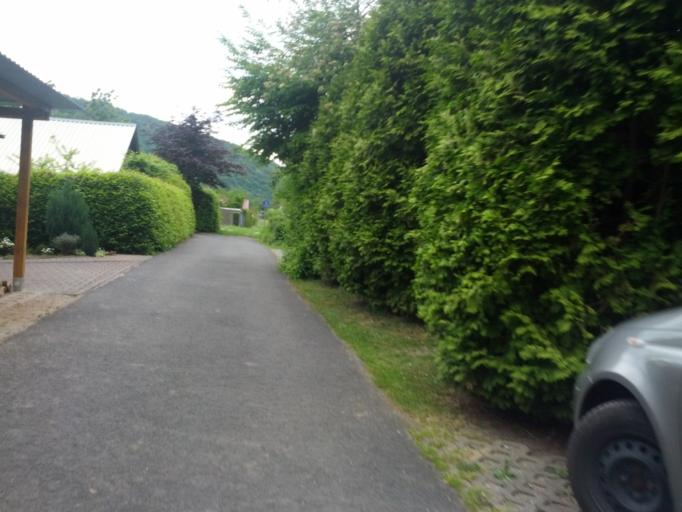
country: DE
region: Thuringia
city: Frankenroda
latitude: 51.0948
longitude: 10.2761
